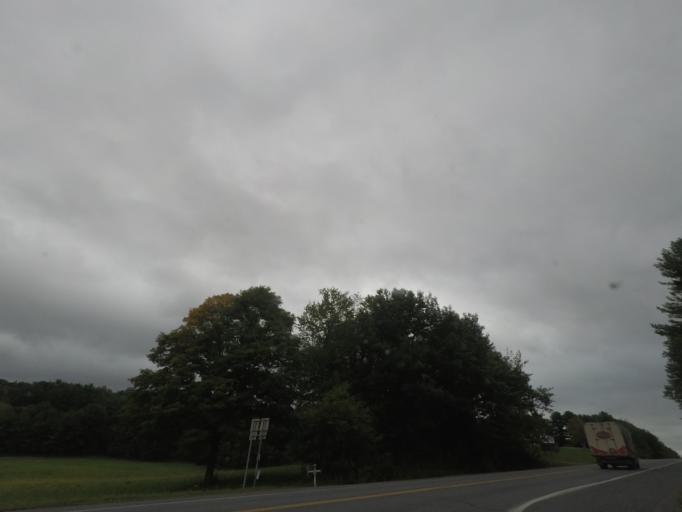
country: US
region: New York
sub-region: Rensselaer County
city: Hoosick Falls
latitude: 42.9514
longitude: -73.3743
